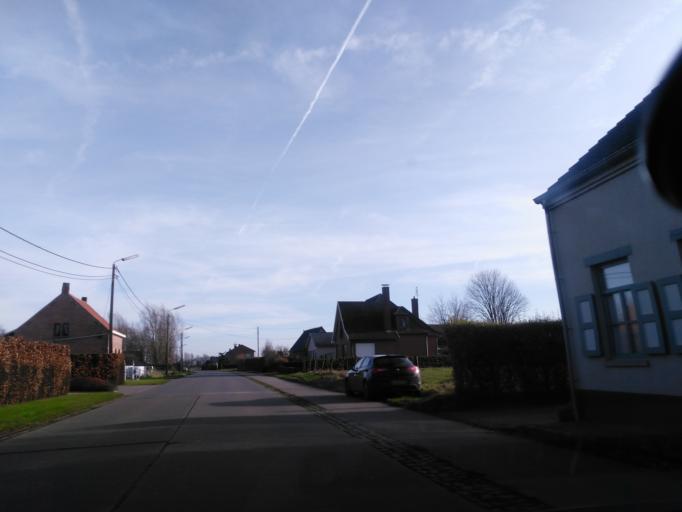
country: BE
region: Flanders
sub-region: Provincie Oost-Vlaanderen
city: Sint-Gillis-Waas
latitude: 51.2263
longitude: 4.1552
